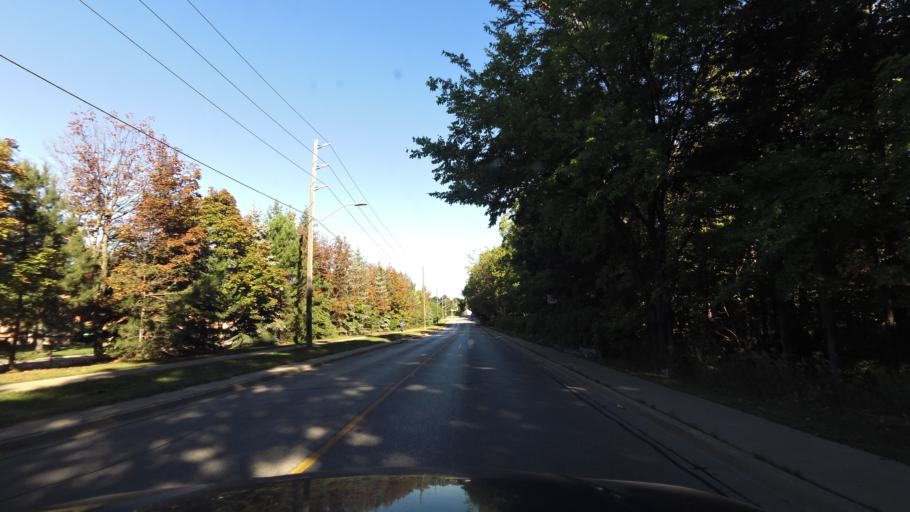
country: CA
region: Ontario
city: Mississauga
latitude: 43.6057
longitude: -79.6752
